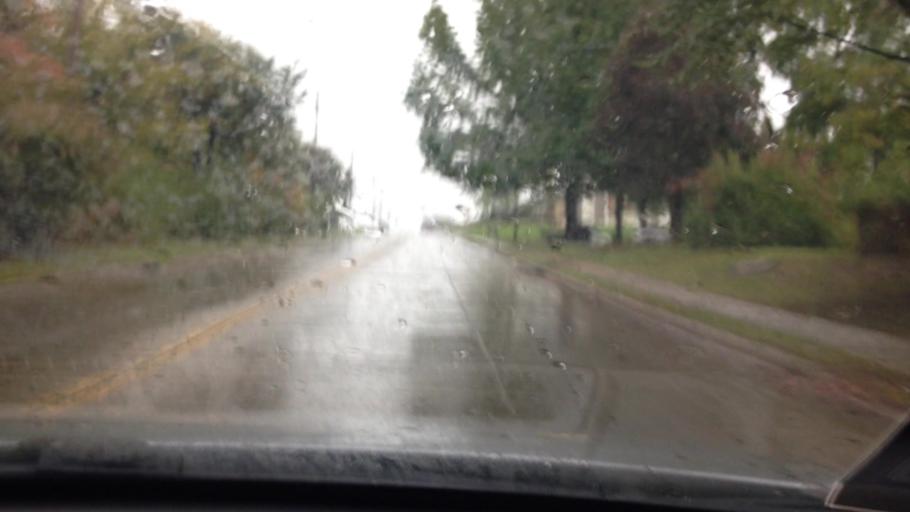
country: US
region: Kansas
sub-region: Leavenworth County
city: Leavenworth
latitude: 39.2861
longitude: -94.9091
